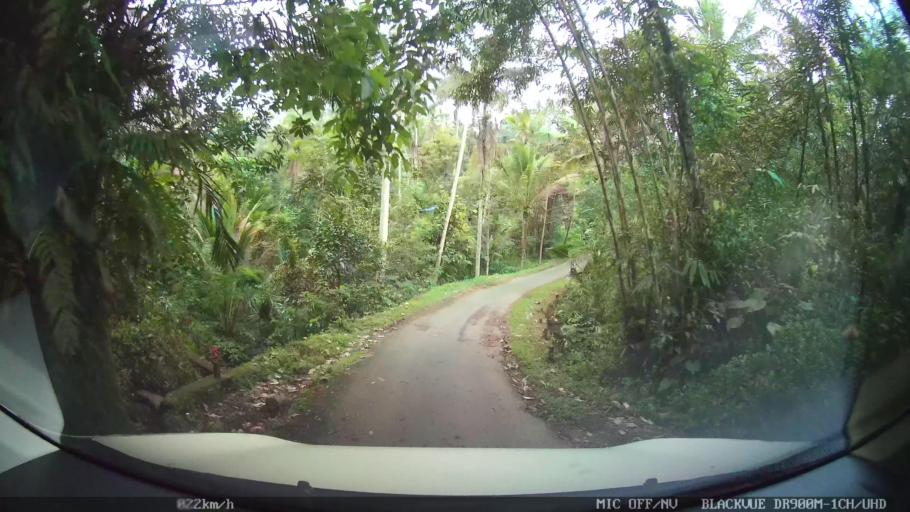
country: ID
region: Bali
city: Banjar Wangsian
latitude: -8.4576
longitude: 115.4120
